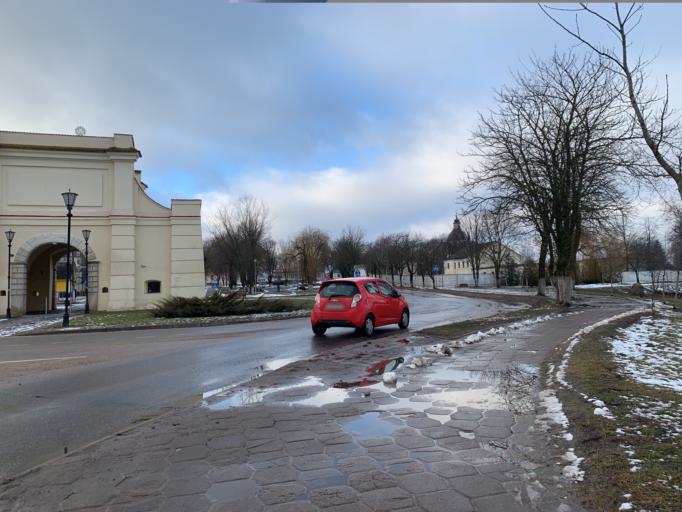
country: BY
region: Minsk
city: Nyasvizh
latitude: 53.2178
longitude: 26.6861
